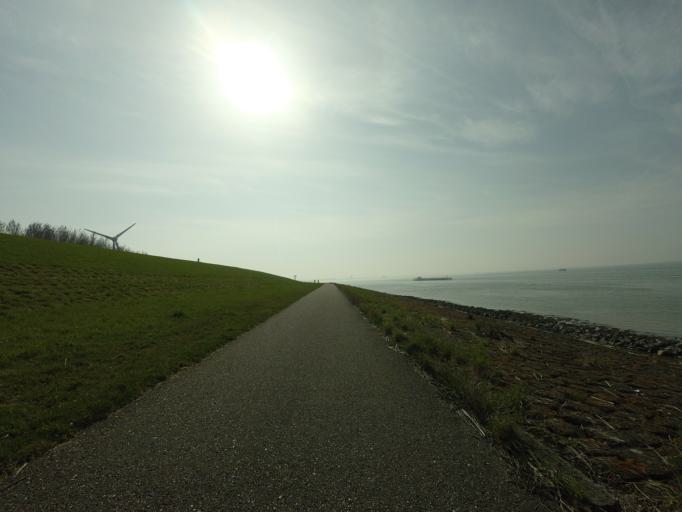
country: NL
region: Zeeland
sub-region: Gemeente Terneuzen
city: Zaamslag
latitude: 51.3575
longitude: 3.9066
